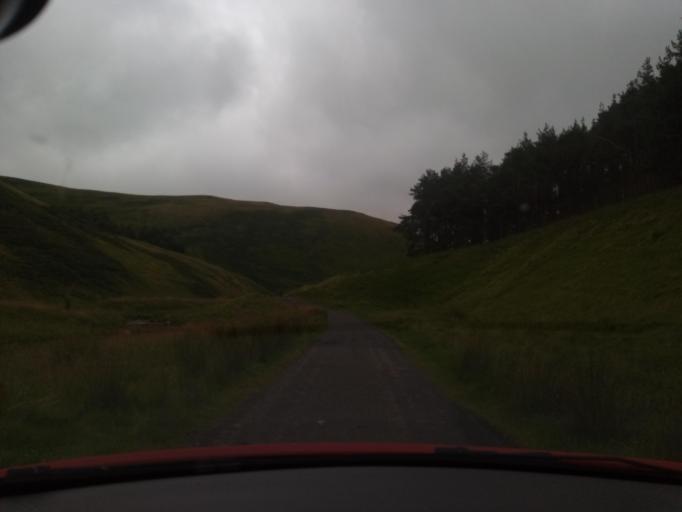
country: GB
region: England
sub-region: Northumberland
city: Rochester
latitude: 55.3978
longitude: -2.2491
